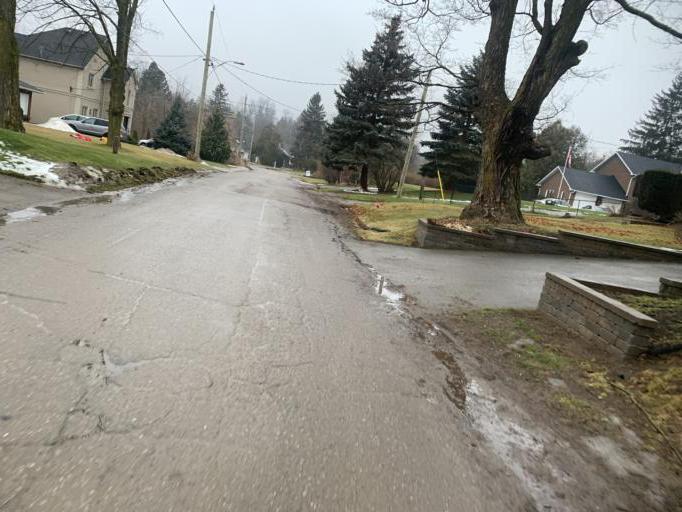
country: CA
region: Ontario
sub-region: Halton
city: Milton
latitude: 43.6601
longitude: -79.9329
